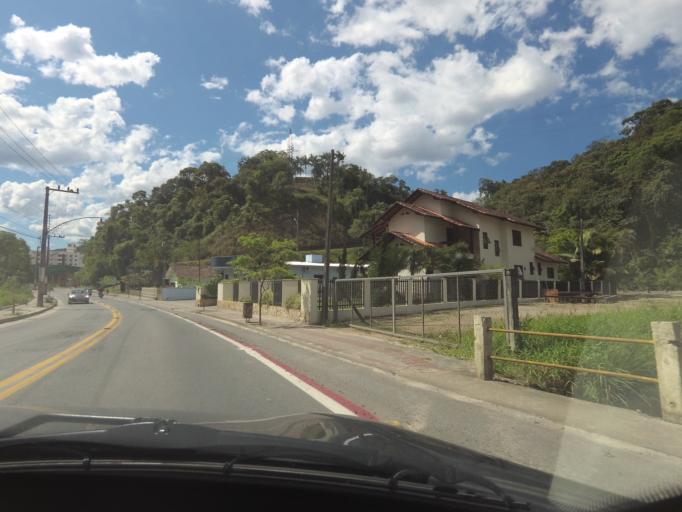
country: BR
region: Santa Catarina
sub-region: Brusque
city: Brusque
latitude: -27.0764
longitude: -48.9174
